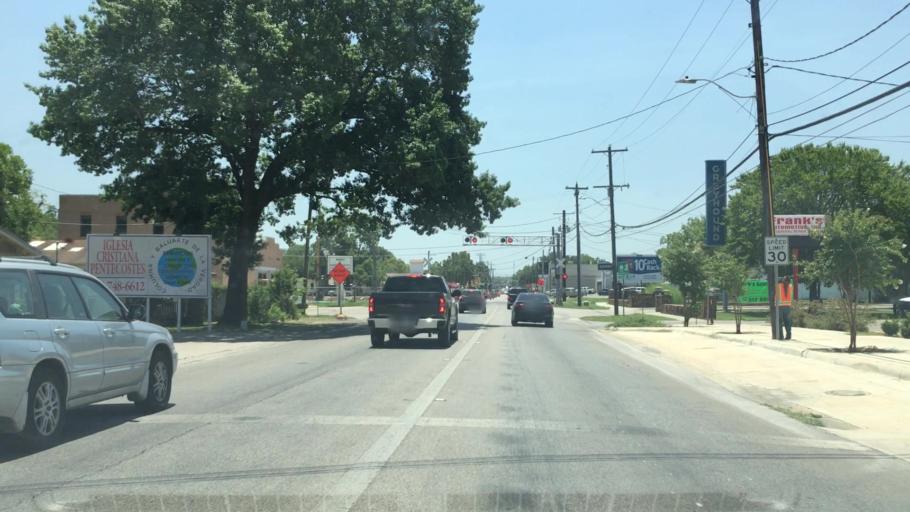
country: US
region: Texas
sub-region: Hays County
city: San Marcos
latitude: 29.8775
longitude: -97.9405
